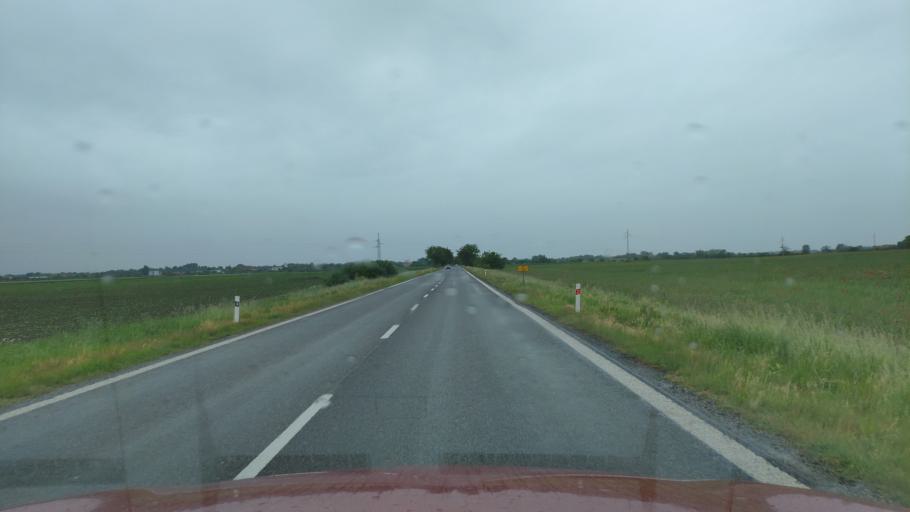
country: HU
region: Borsod-Abauj-Zemplen
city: Karcsa
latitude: 48.4199
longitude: 21.8348
